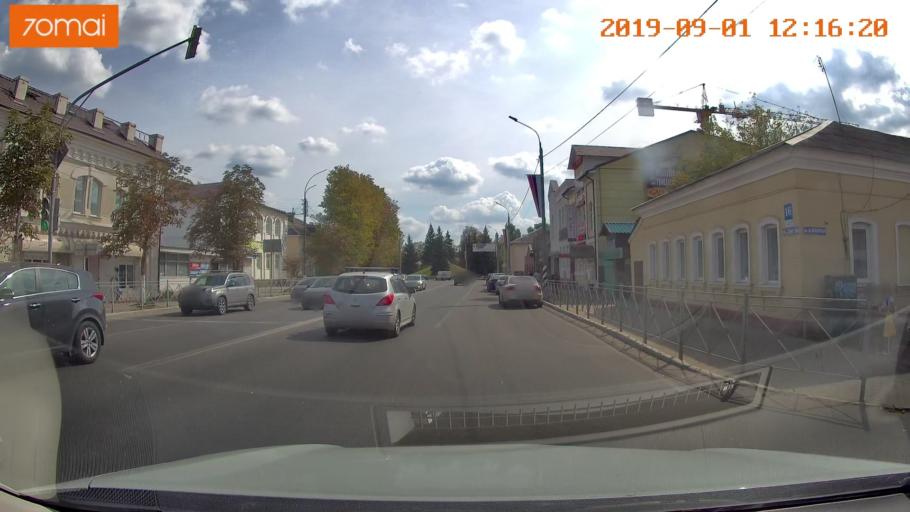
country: RU
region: Kaluga
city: Maloyaroslavets
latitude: 55.0104
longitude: 36.4651
